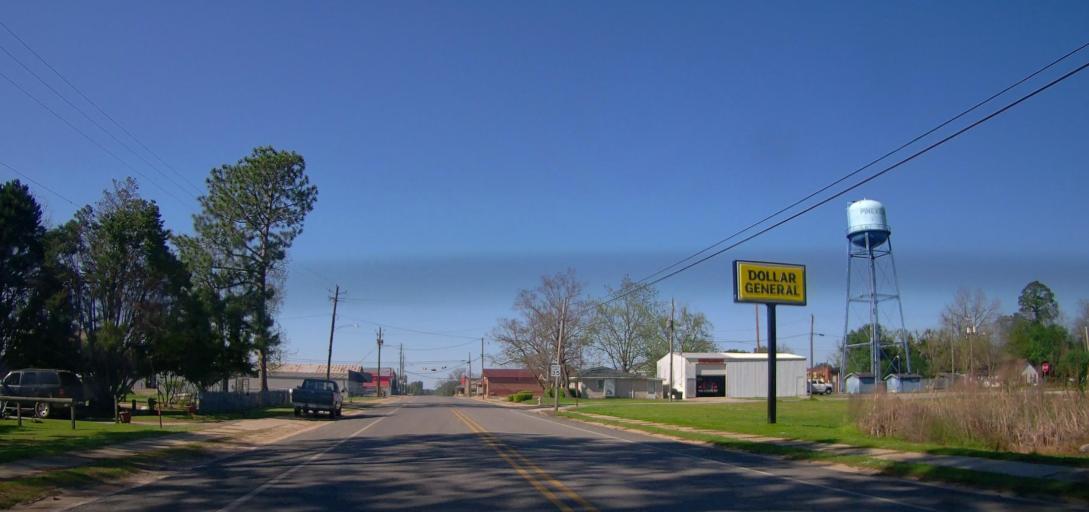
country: US
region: Georgia
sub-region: Wilcox County
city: Rochelle
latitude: 32.1090
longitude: -83.5011
